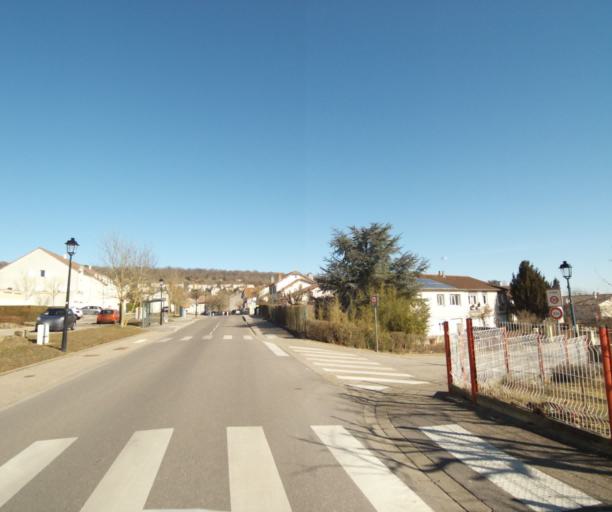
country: FR
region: Lorraine
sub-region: Departement de Meurthe-et-Moselle
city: Ludres
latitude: 48.6187
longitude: 6.1593
